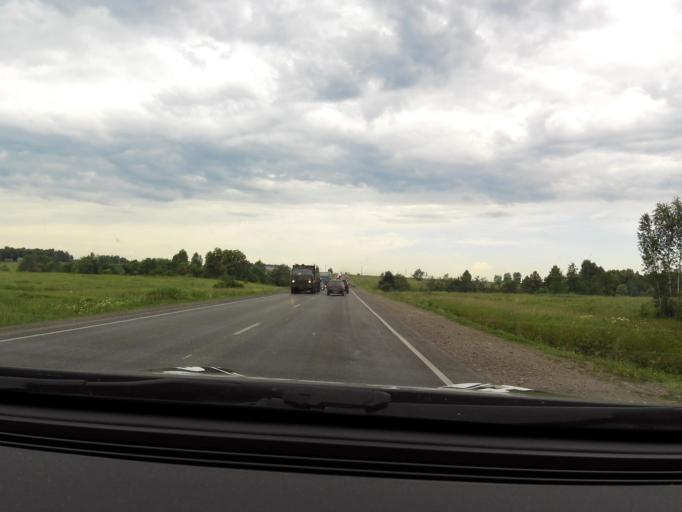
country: RU
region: Bashkortostan
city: Kudeyevskiy
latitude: 54.8171
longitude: 56.7746
